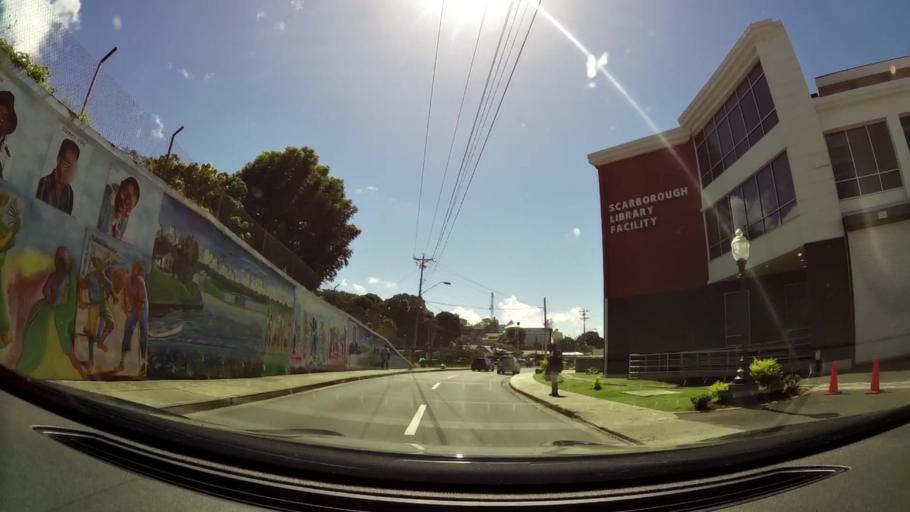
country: TT
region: Tobago
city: Scarborough
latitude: 11.1842
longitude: -60.7361
